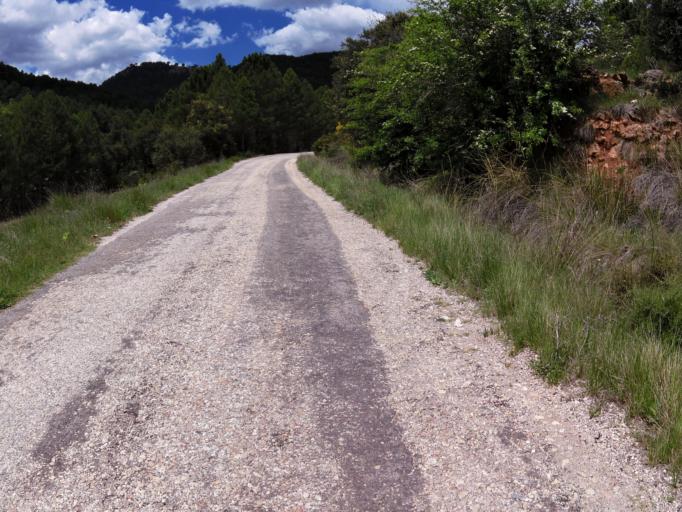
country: ES
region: Castille-La Mancha
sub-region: Provincia de Albacete
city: Paterna del Madera
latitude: 38.5794
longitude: -2.3426
